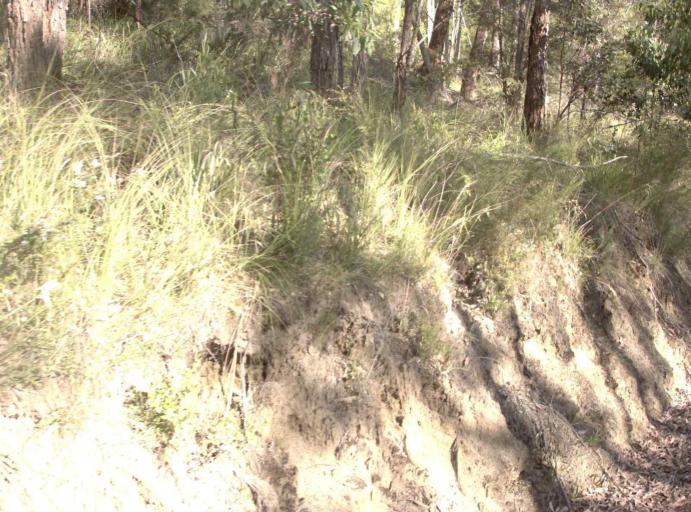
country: AU
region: Victoria
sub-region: East Gippsland
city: Lakes Entrance
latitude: -37.6243
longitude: 148.5074
